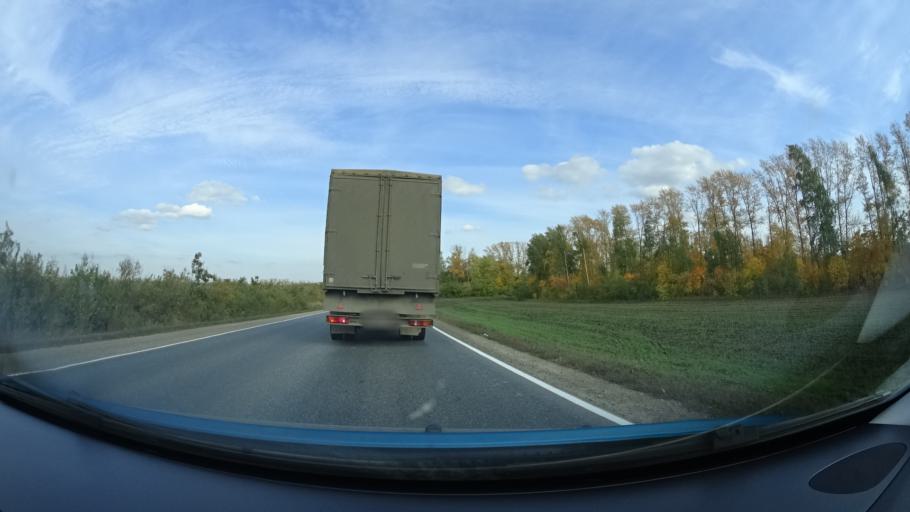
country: RU
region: Bashkortostan
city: Kandry
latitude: 54.5545
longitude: 54.1823
